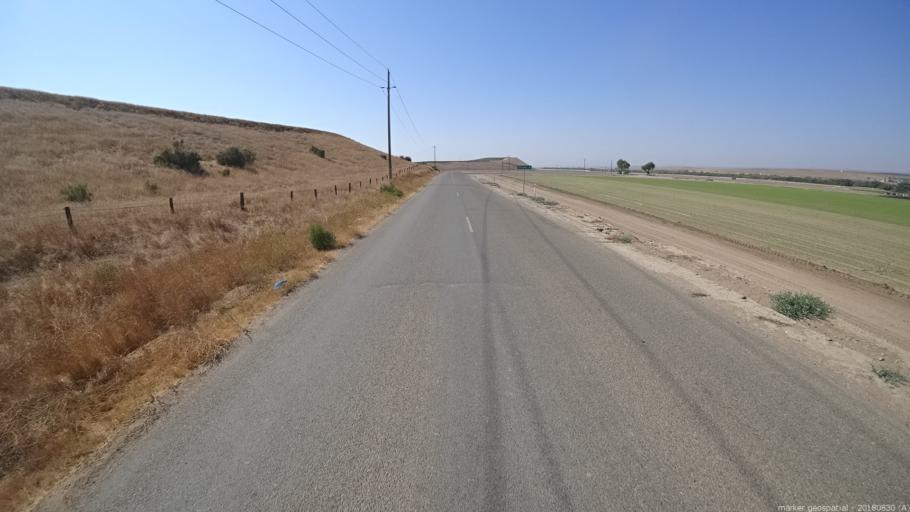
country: US
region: California
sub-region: Monterey County
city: King City
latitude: 36.1095
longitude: -121.0319
